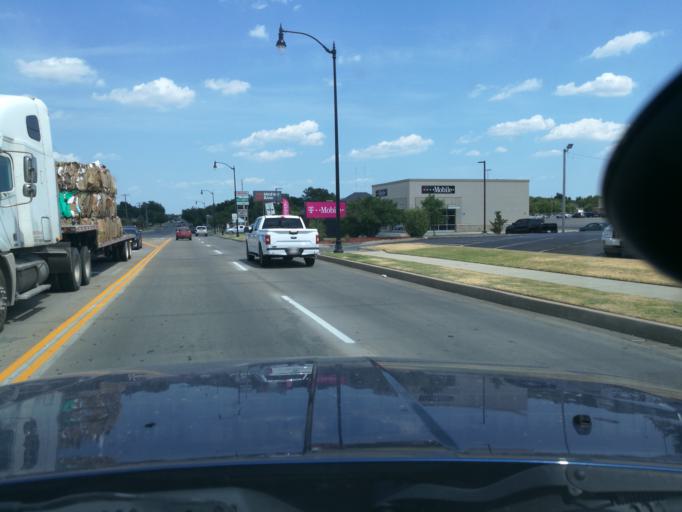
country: US
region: Oklahoma
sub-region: Oklahoma County
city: Oklahoma City
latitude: 35.4207
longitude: -97.5301
